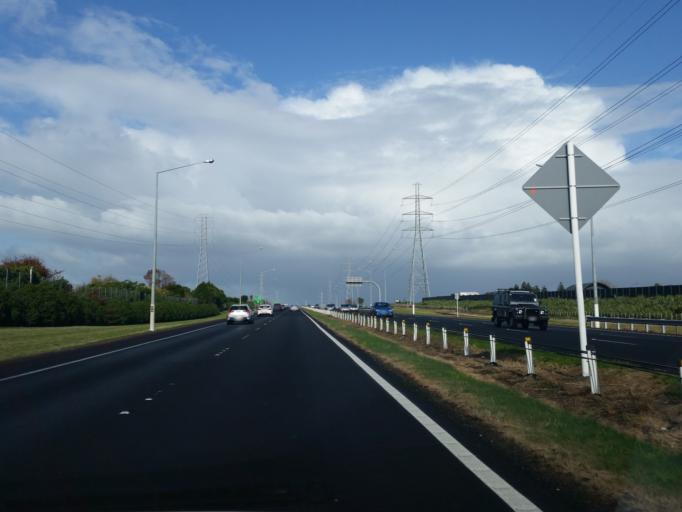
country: NZ
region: Auckland
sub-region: Auckland
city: Papakura
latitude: -37.0648
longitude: 174.9256
